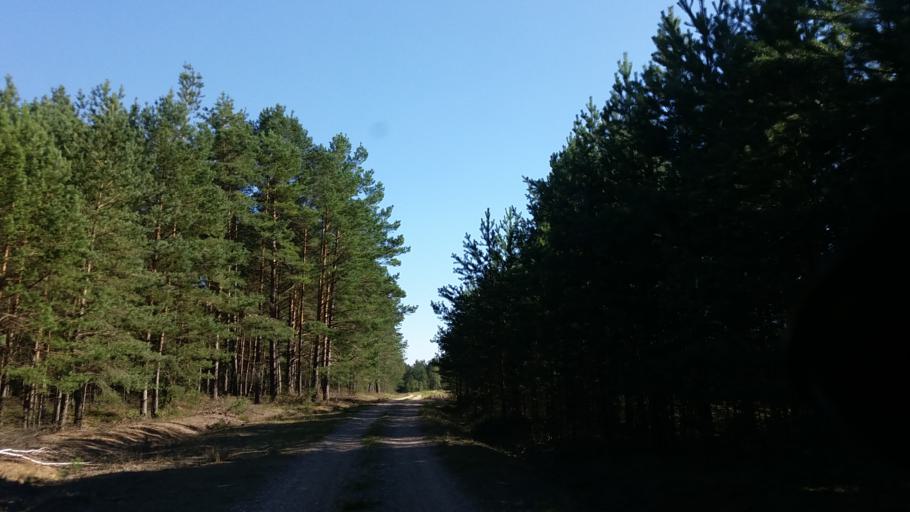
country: PL
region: West Pomeranian Voivodeship
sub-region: Powiat szczecinecki
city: Borne Sulinowo
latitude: 53.5620
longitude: 16.5027
